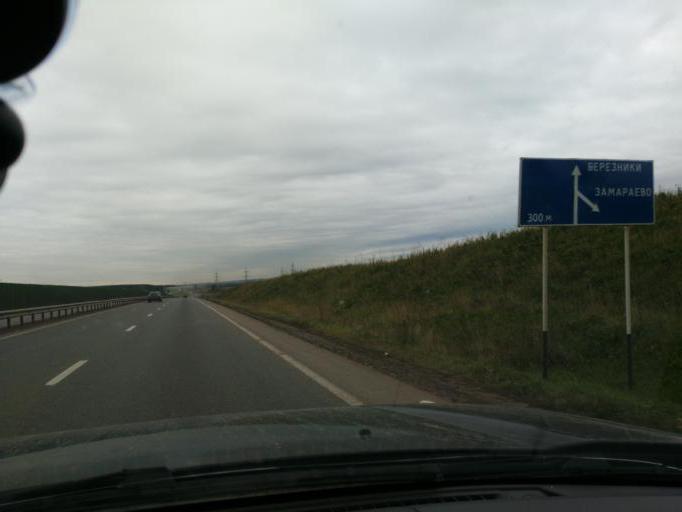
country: RU
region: Perm
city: Froly
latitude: 57.9349
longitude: 56.2238
